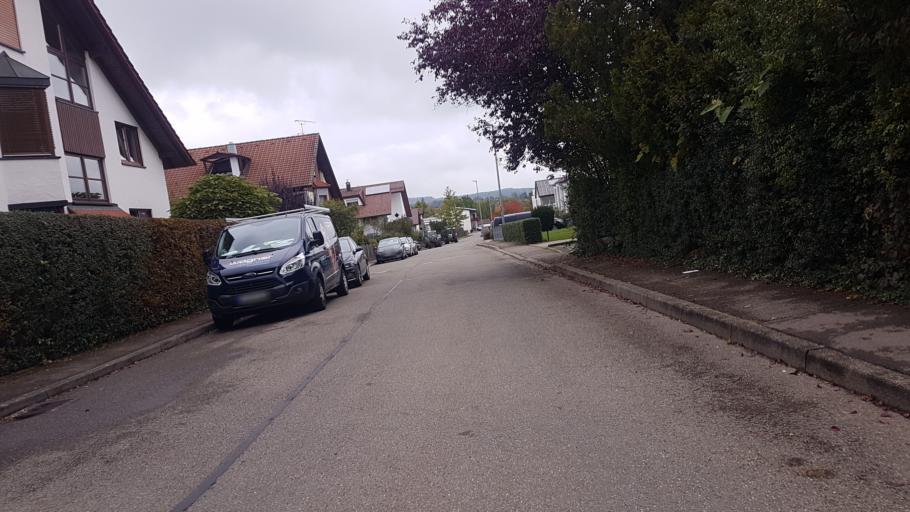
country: DE
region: Baden-Wuerttemberg
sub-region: Tuebingen Region
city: Dusslingen
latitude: 48.4449
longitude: 9.0557
